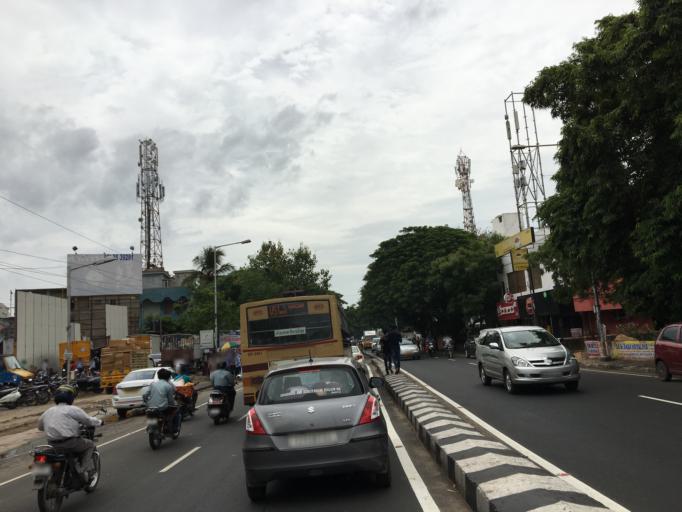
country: IN
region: Tamil Nadu
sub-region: Kancheepuram
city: Alandur
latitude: 12.9935
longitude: 80.2182
